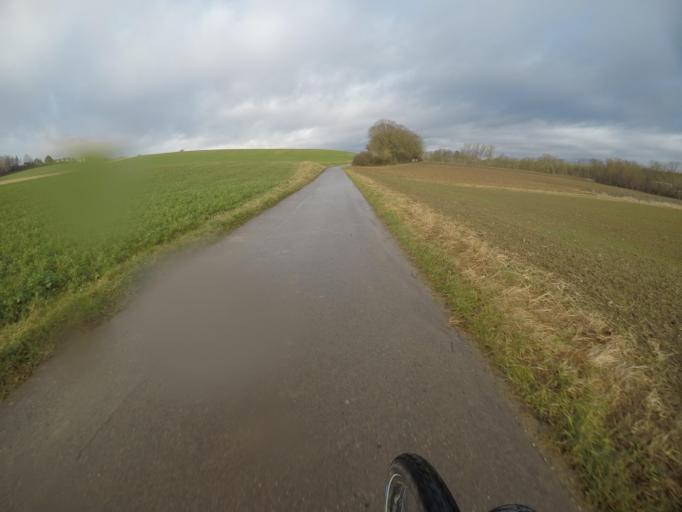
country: DE
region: Baden-Wuerttemberg
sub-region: Regierungsbezirk Stuttgart
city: Ditzingen
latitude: 48.8387
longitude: 9.0545
